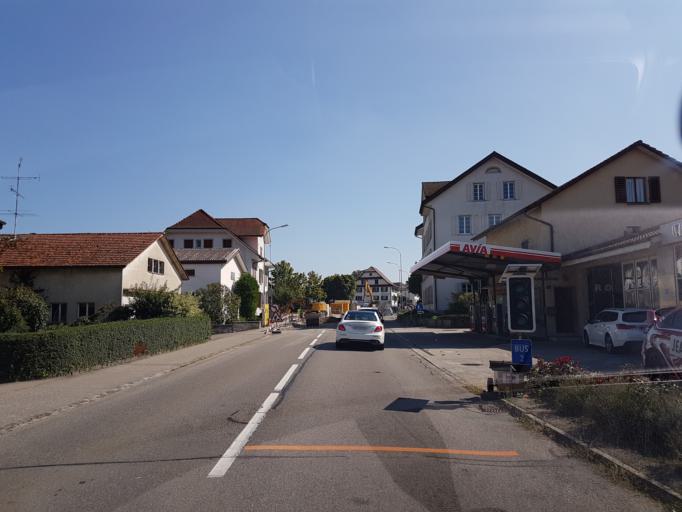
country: CH
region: Aargau
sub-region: Bezirk Muri
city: Waltenschwil
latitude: 47.3032
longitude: 8.3120
